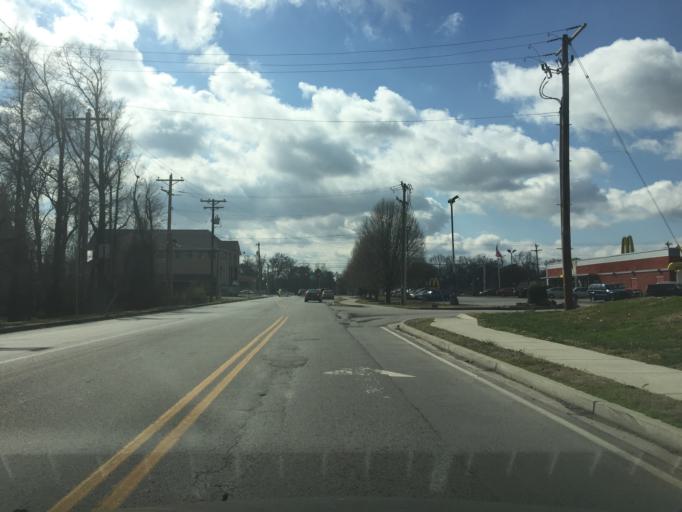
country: US
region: Georgia
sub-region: Catoosa County
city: Fort Oglethorpe
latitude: 34.9536
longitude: -85.2438
